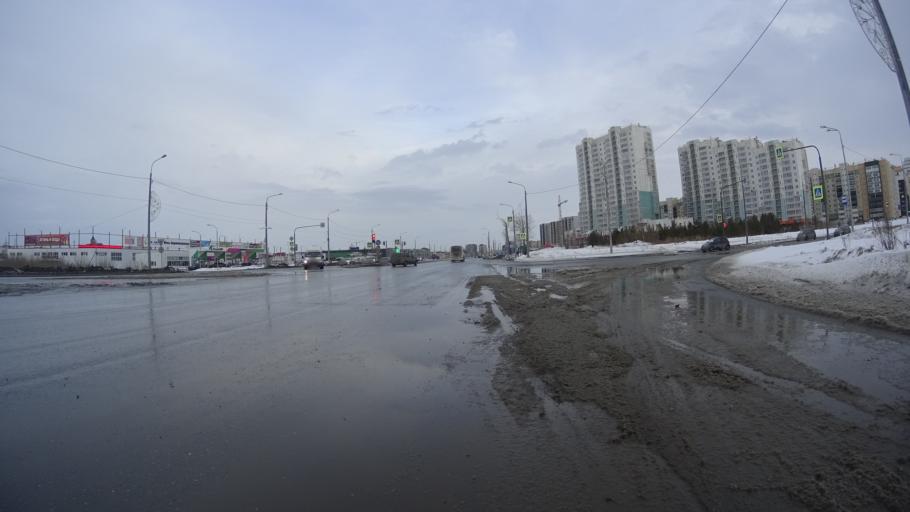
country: RU
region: Chelyabinsk
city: Roshchino
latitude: 55.1790
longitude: 61.2567
